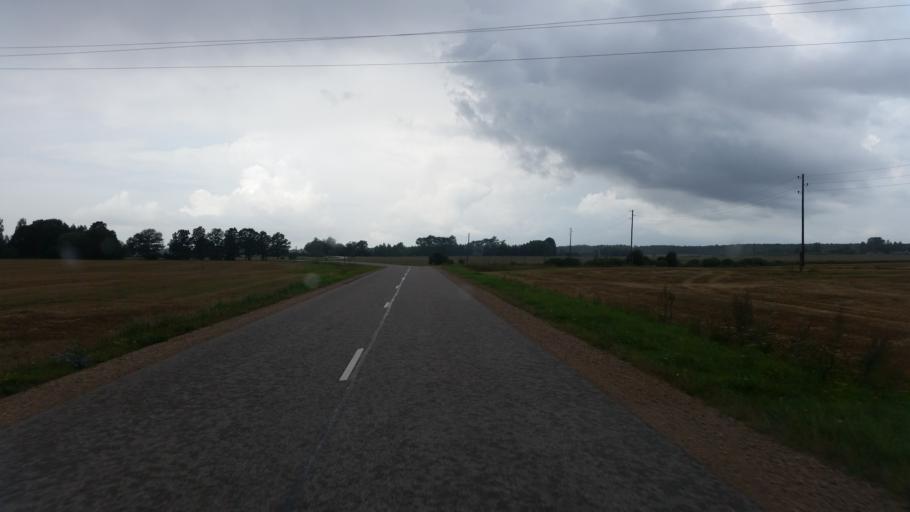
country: LV
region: Vecumnieki
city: Vecumnieki
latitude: 56.4335
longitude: 24.4252
